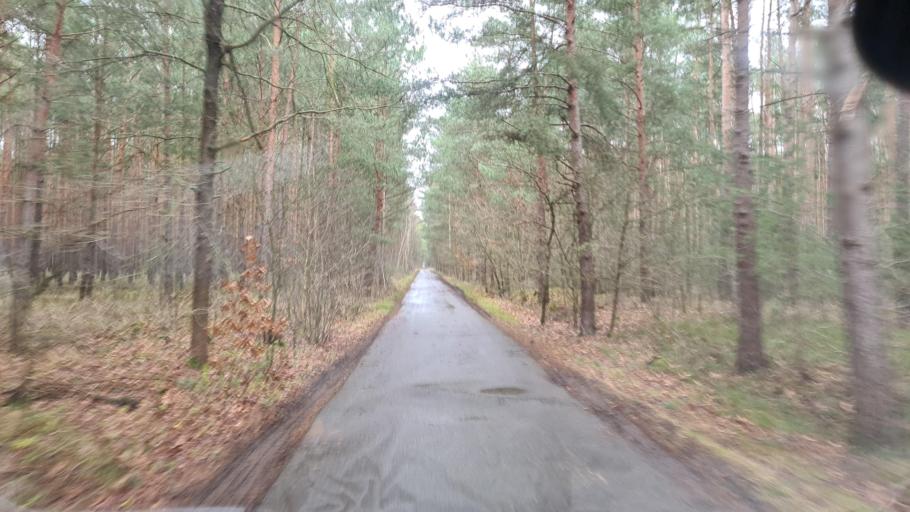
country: DE
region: Brandenburg
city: Kroppen
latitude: 51.4055
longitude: 13.7786
